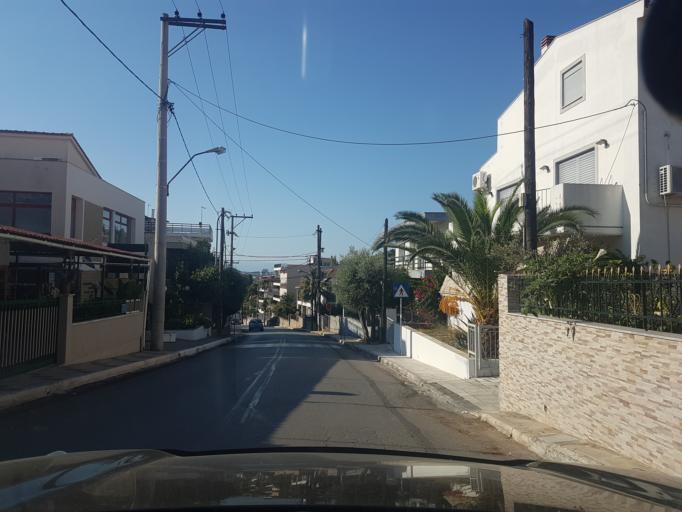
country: GR
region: Central Greece
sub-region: Nomos Evvoias
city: Chalkida
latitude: 38.4700
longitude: 23.5865
